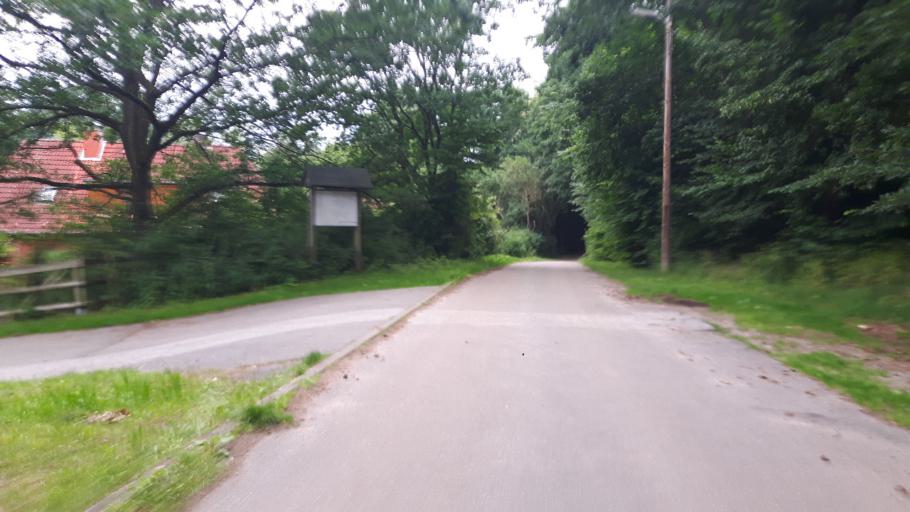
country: DE
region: Schleswig-Holstein
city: Ratekau
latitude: 53.9149
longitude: 10.7848
